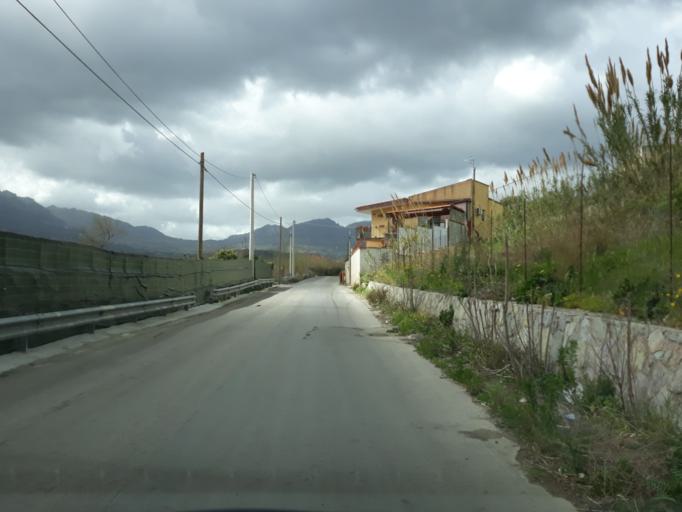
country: IT
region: Sicily
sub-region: Palermo
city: Monreale
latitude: 38.0791
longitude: 13.2931
